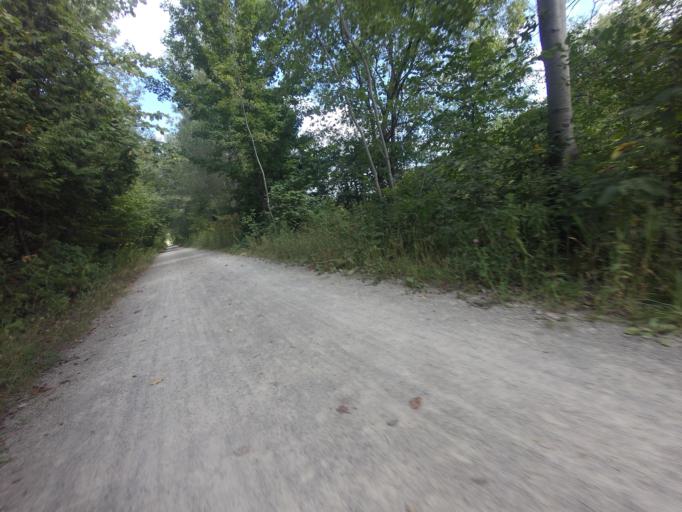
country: CA
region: Ontario
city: Uxbridge
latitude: 44.1250
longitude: -79.1100
